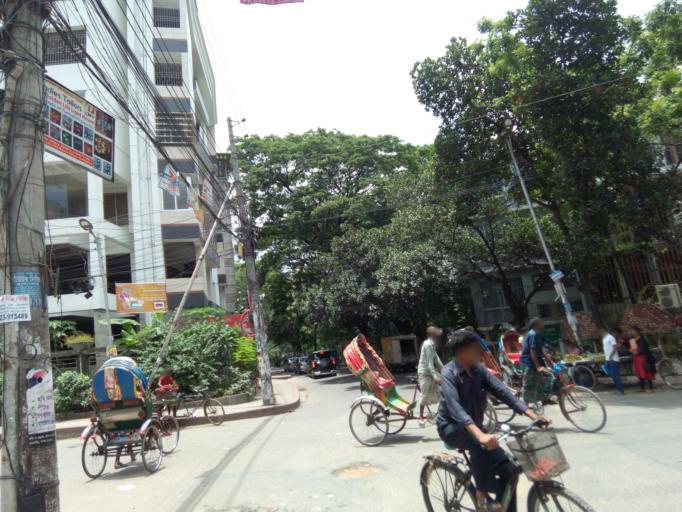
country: BD
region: Dhaka
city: Azimpur
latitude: 23.7500
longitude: 90.3746
